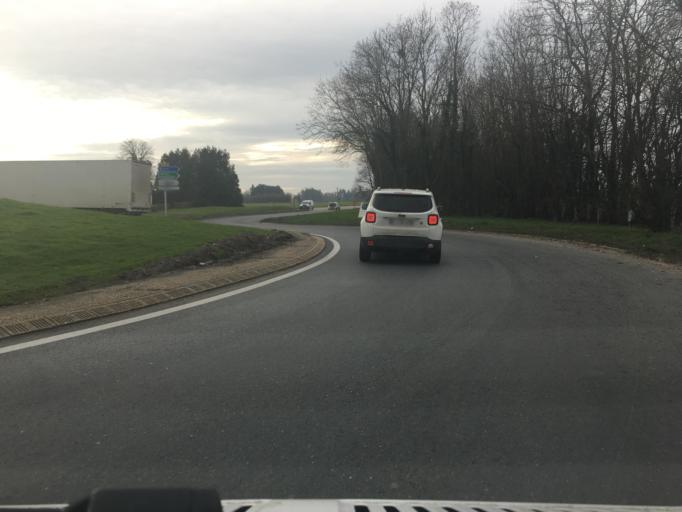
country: FR
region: Haute-Normandie
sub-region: Departement de l'Eure
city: Beuzeville
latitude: 49.3587
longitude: 0.3941
